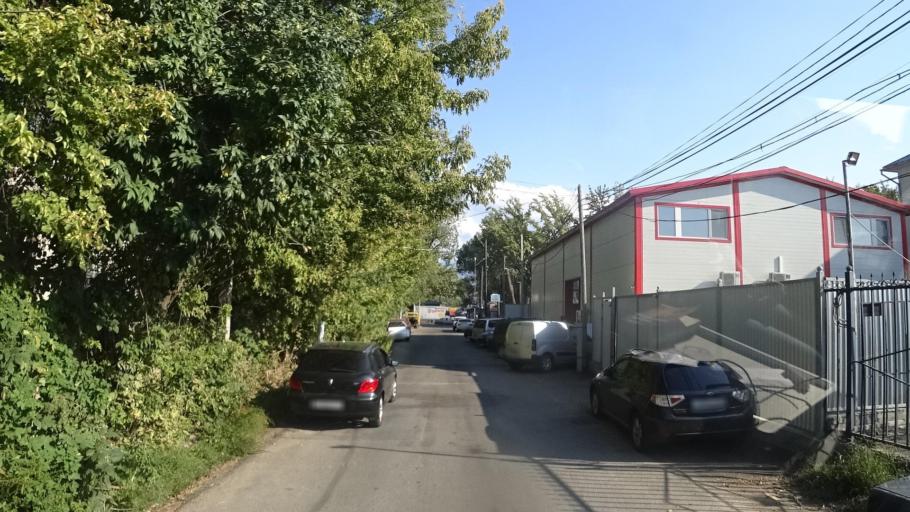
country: KZ
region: Almaty Qalasy
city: Almaty
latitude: 43.2884
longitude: 76.9229
